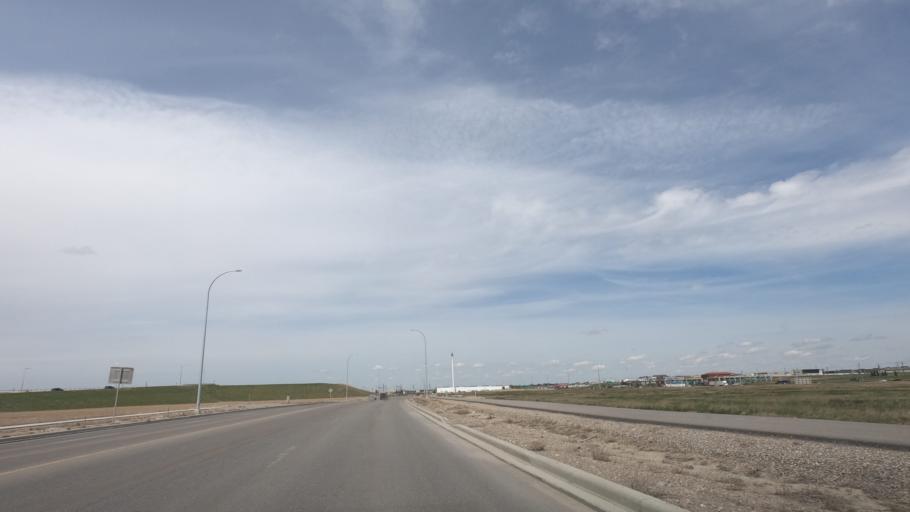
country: CA
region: Alberta
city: Airdrie
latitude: 51.2534
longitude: -114.0049
